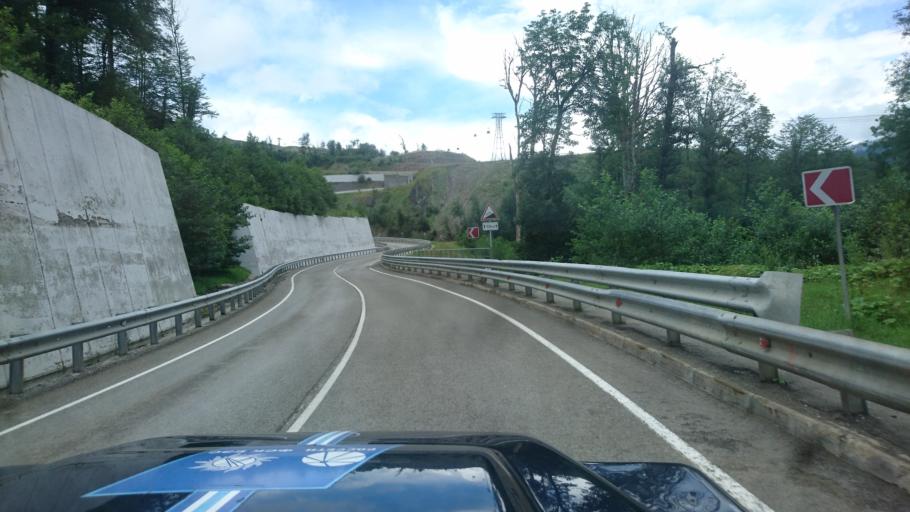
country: RU
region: Krasnodarskiy
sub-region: Sochi City
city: Krasnaya Polyana
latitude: 43.6508
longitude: 40.3319
